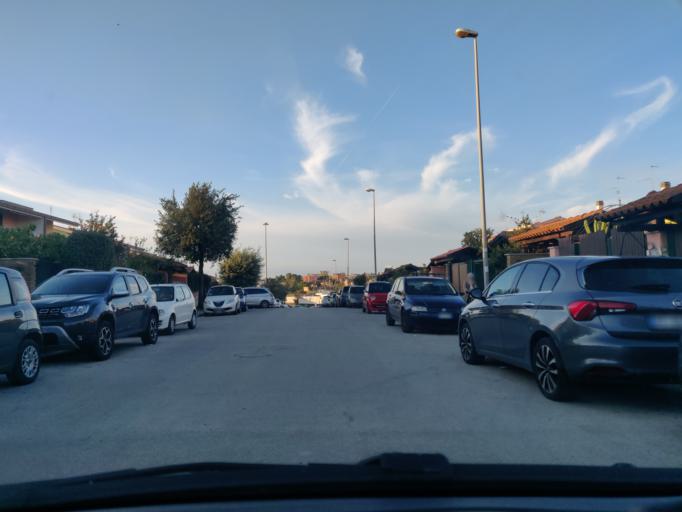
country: IT
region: Latium
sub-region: Citta metropolitana di Roma Capitale
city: Civitavecchia
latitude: 42.0644
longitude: 11.8202
